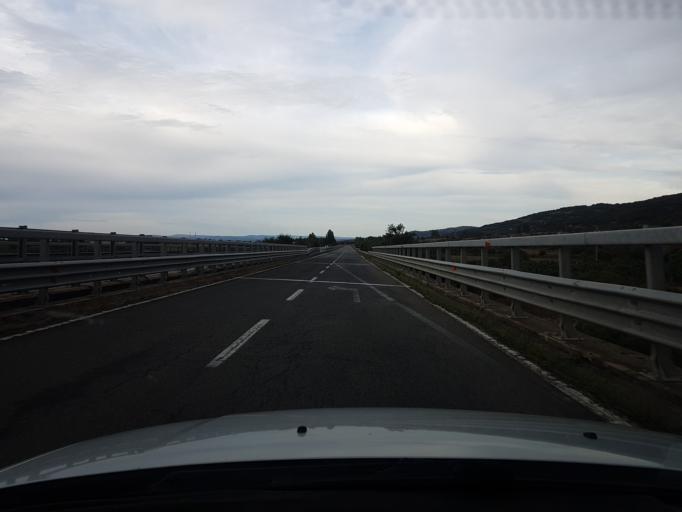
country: IT
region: Sardinia
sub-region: Provincia di Oristano
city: Sedilo
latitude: 40.1806
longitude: 8.9608
